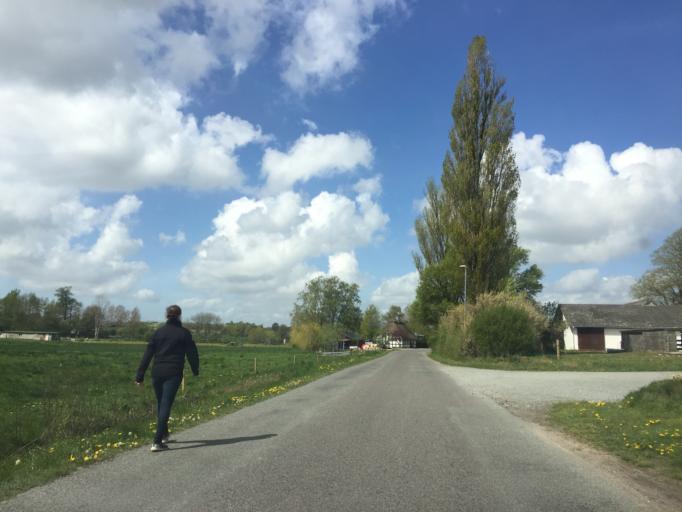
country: DK
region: South Denmark
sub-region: Faaborg-Midtfyn Kommune
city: Ringe
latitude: 55.2143
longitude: 10.5662
